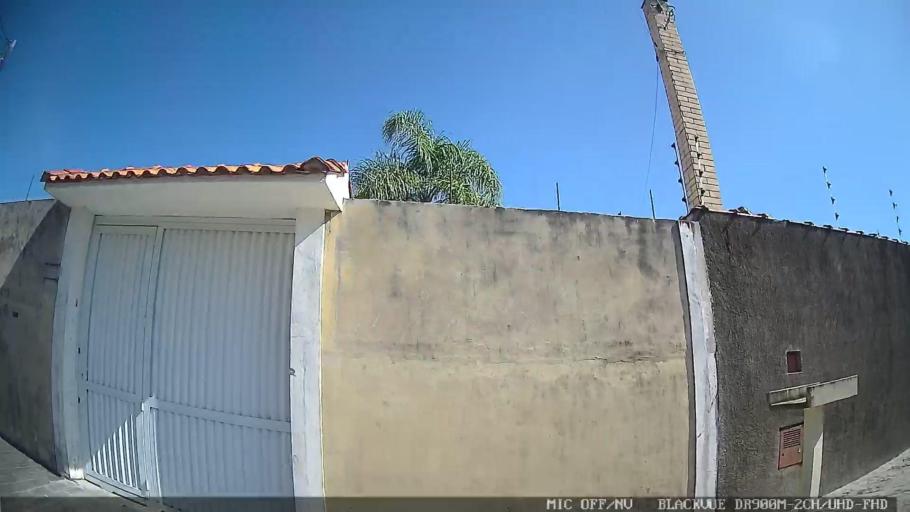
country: BR
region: Sao Paulo
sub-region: Peruibe
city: Peruibe
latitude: -24.2749
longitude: -46.9434
